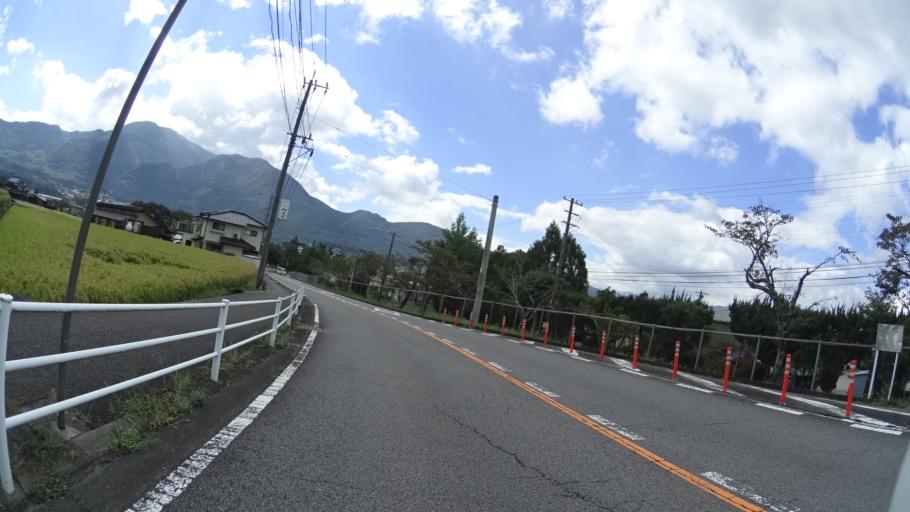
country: JP
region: Oita
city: Beppu
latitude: 33.2698
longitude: 131.3616
